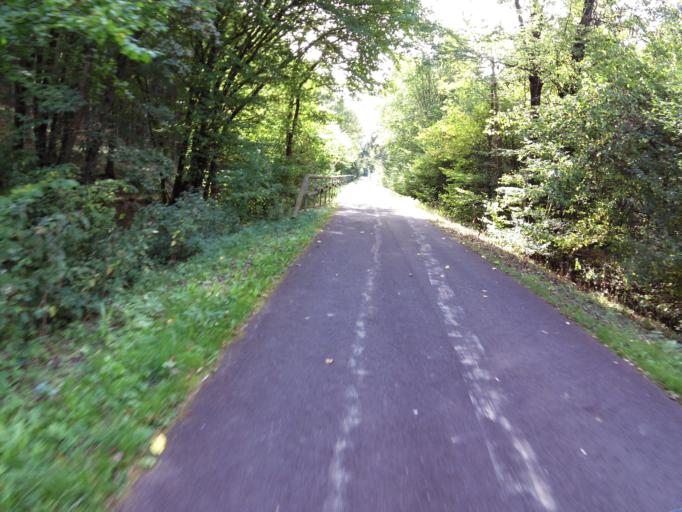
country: DE
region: Rheinland-Pfalz
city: Winterscheid
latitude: 50.2278
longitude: 6.2562
